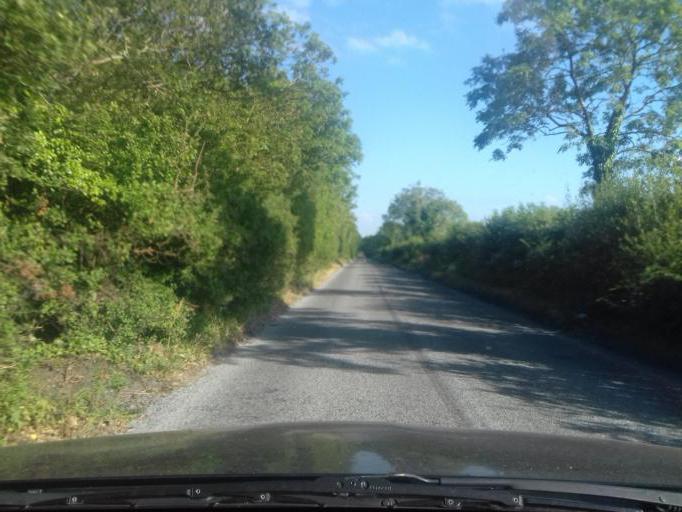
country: IE
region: Leinster
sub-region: Fingal County
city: Blanchardstown
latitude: 53.4408
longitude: -6.3851
